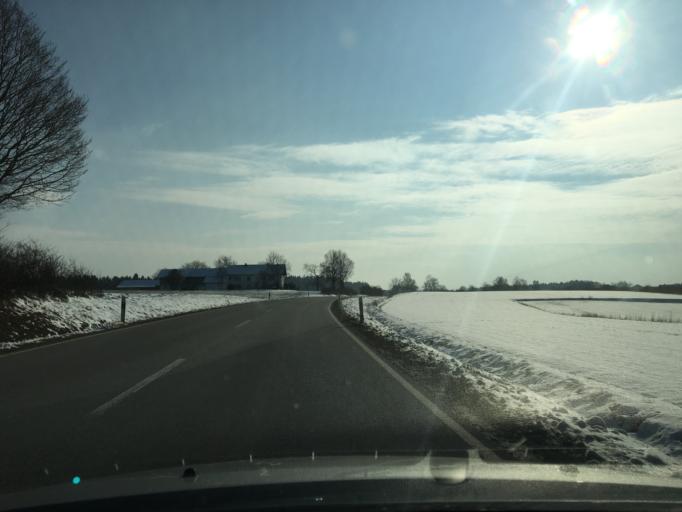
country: DE
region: Bavaria
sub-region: Lower Bavaria
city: Gangkofen
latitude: 48.4245
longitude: 12.5579
